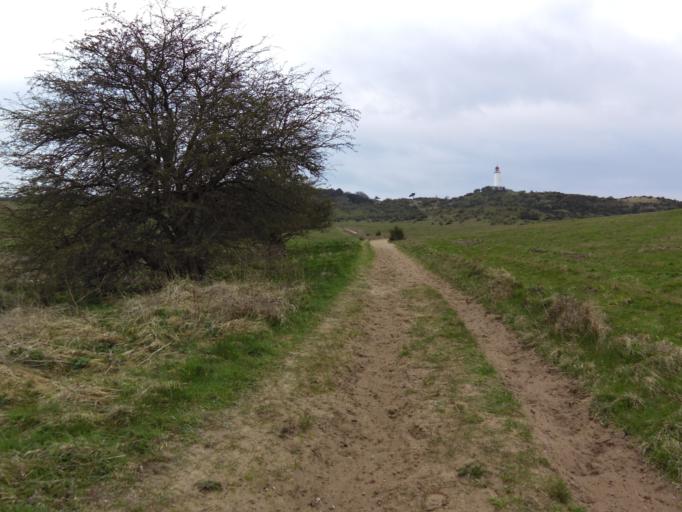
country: DE
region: Mecklenburg-Vorpommern
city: Hiddensee
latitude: 54.5980
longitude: 13.1275
